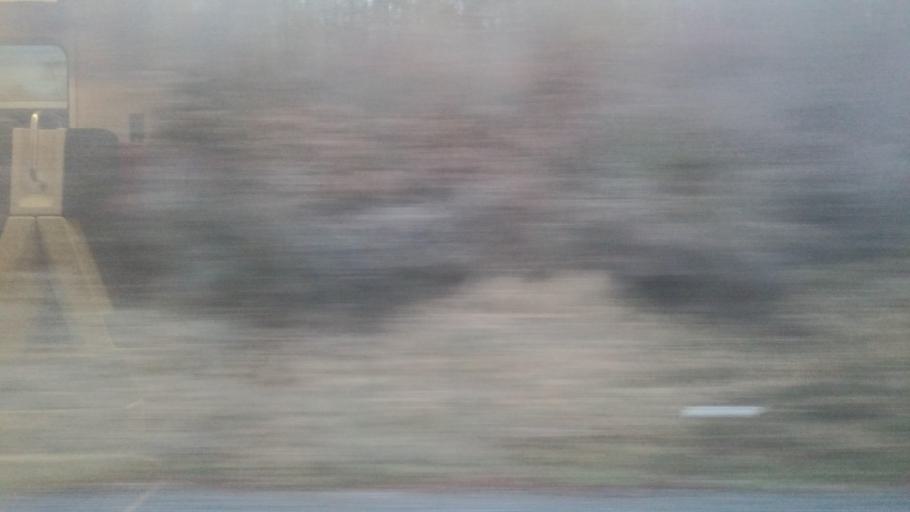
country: CH
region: Aargau
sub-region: Bezirk Brugg
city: Schinznach Dorf
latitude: 47.4592
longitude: 8.1481
